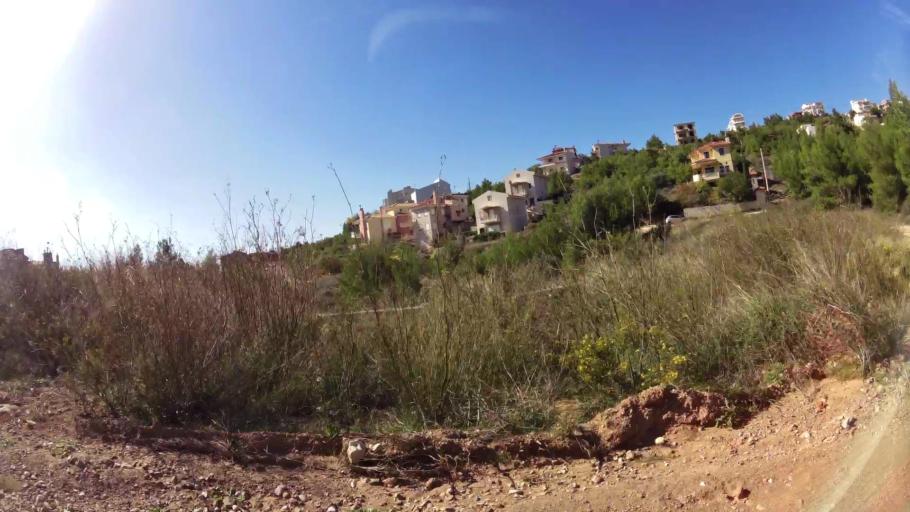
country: GR
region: Attica
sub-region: Nomarchia Anatolikis Attikis
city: Dioni
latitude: 38.0340
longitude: 23.9348
